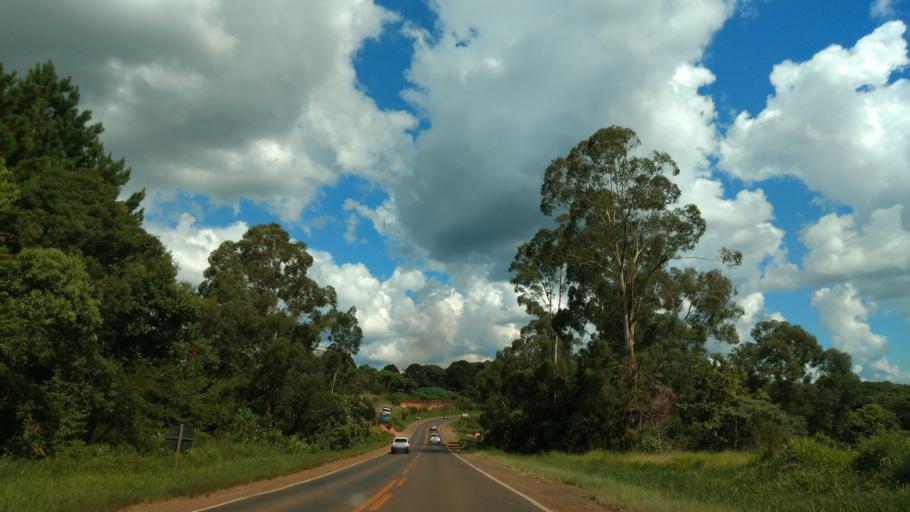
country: BR
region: Parana
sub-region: Guarapuava
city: Guarapuava
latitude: -25.4218
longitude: -51.4925
